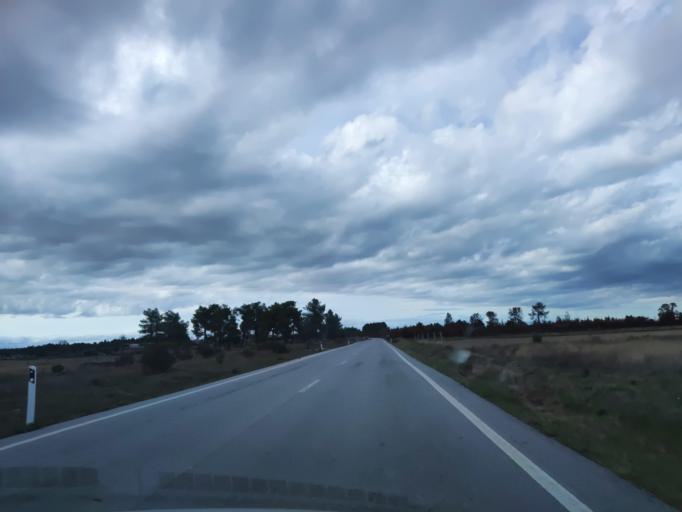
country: ES
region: Castille and Leon
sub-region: Provincia de Salamanca
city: Aldea del Obispo
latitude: 40.6659
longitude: -6.8582
